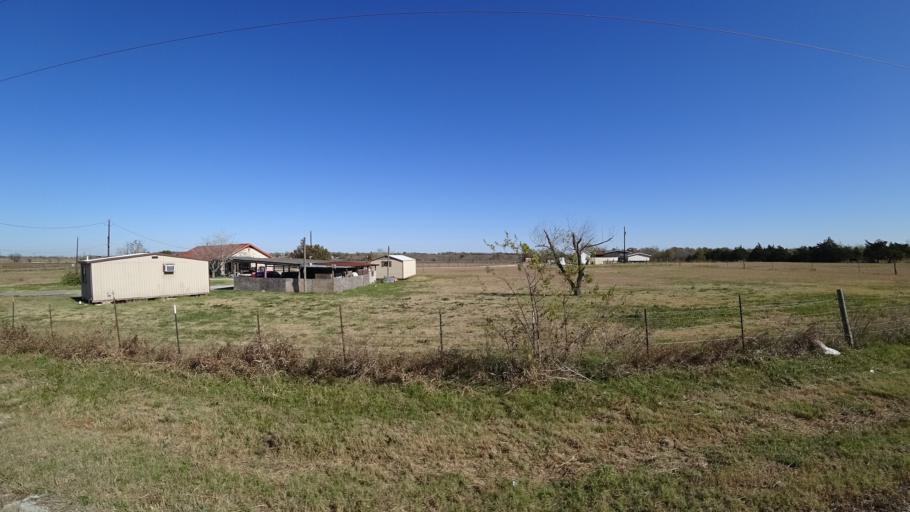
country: US
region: Texas
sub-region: Travis County
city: Garfield
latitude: 30.1101
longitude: -97.6497
